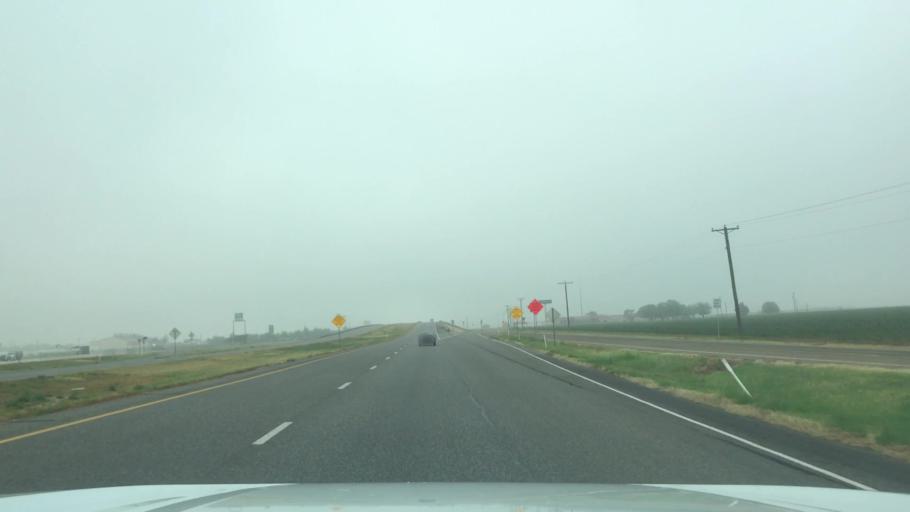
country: US
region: Texas
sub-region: Lubbock County
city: Slaton
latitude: 33.4538
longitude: -101.6664
